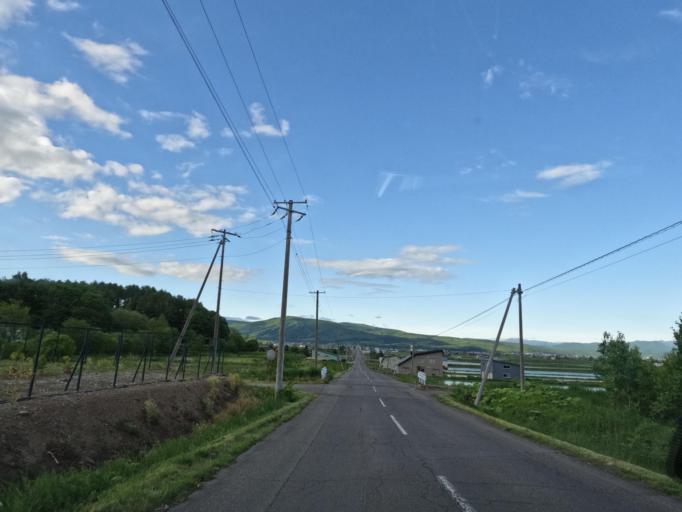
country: JP
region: Hokkaido
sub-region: Asahikawa-shi
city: Asahikawa
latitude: 43.8833
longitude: 142.4571
